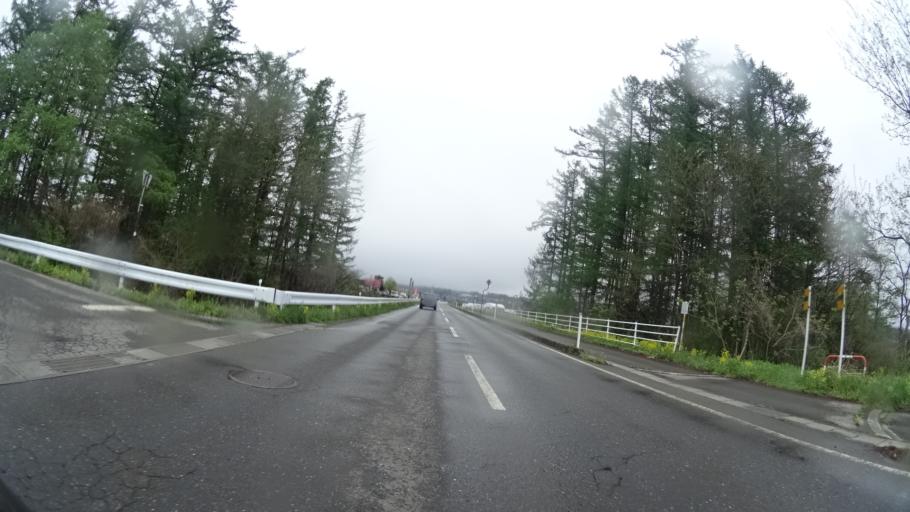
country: JP
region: Nagano
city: Nagano-shi
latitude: 36.7939
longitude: 138.1956
